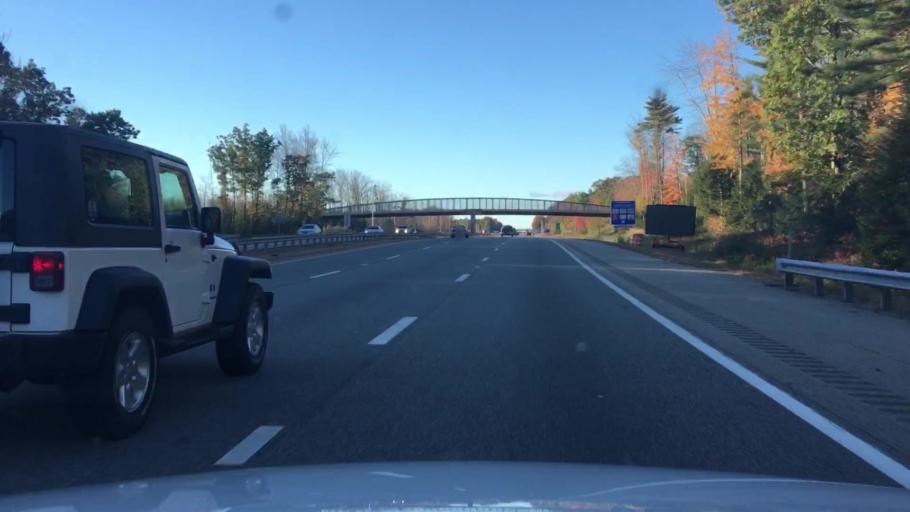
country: US
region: Maine
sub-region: York County
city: West Kennebunk
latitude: 43.4187
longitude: -70.5551
